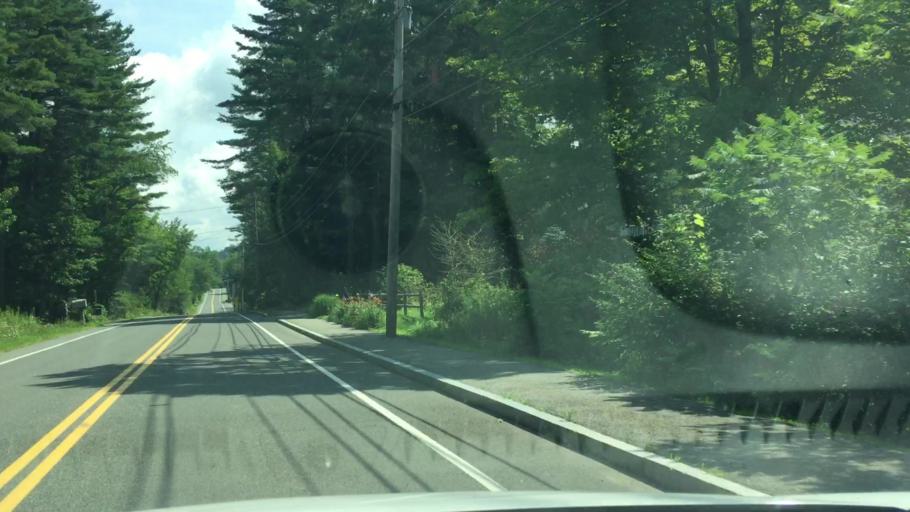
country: US
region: Massachusetts
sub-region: Berkshire County
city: Lenox
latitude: 42.3536
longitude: -73.3080
